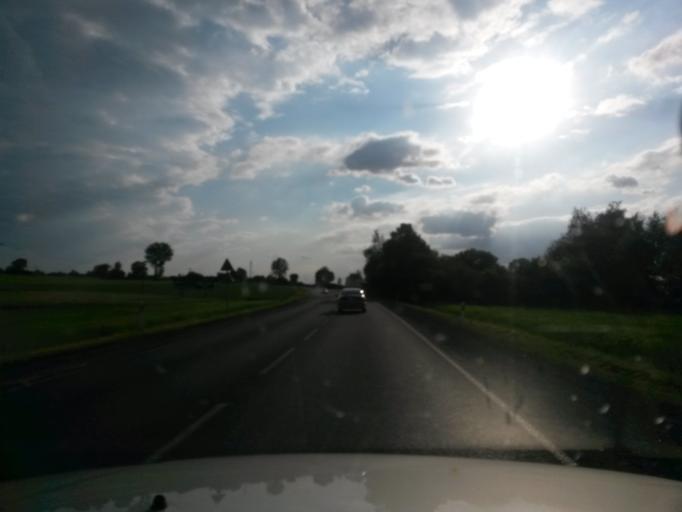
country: PL
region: Lodz Voivodeship
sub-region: Powiat piotrkowski
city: Grabica
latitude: 51.4222
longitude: 19.4956
